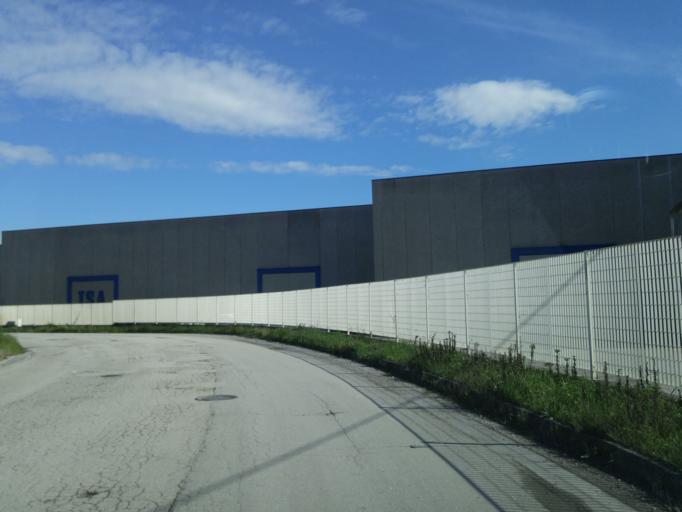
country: IT
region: The Marches
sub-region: Provincia di Pesaro e Urbino
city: Calcinelli
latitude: 43.7430
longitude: 12.9158
